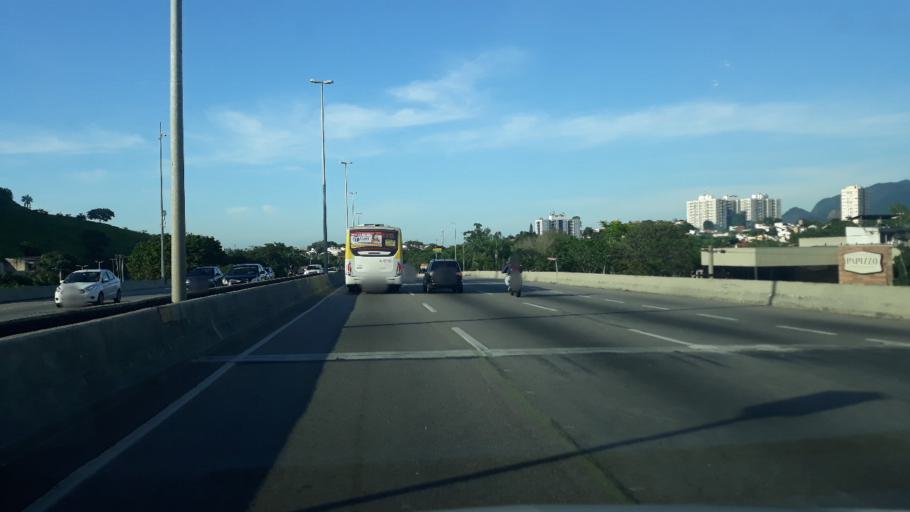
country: BR
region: Rio de Janeiro
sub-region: Sao Joao De Meriti
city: Sao Joao de Meriti
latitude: -22.9381
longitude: -43.3491
